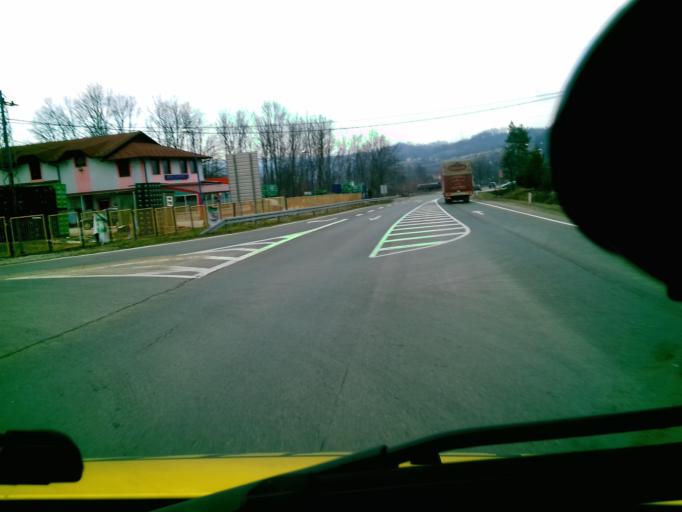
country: BA
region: Federation of Bosnia and Herzegovina
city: Lijesnica
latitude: 44.4788
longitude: 18.0679
